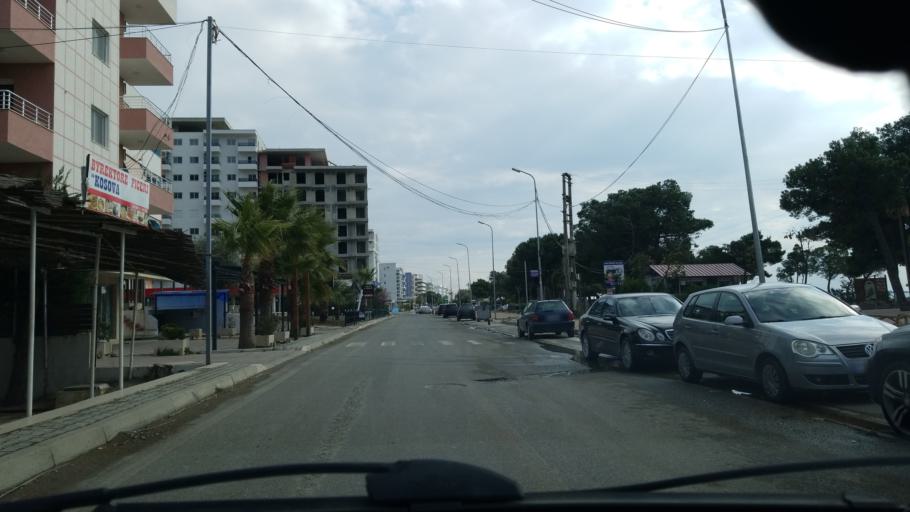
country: AL
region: Lezhe
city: Shengjin
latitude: 41.8050
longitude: 19.6000
